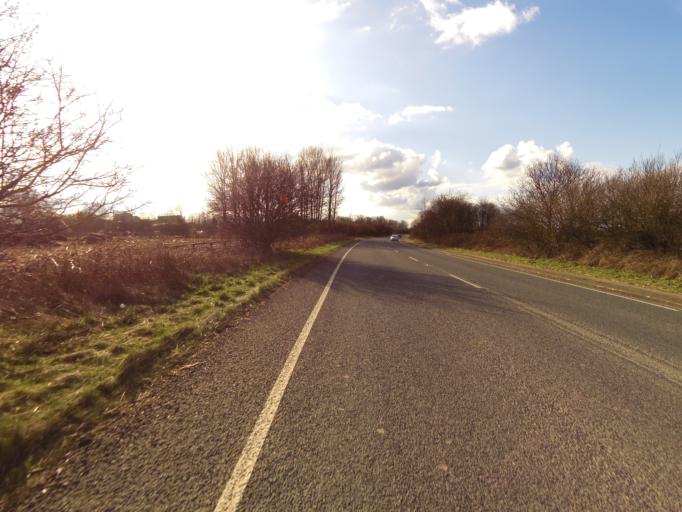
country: GB
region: England
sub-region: East Riding of Yorkshire
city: Pollington
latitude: 53.6821
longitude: -1.0592
